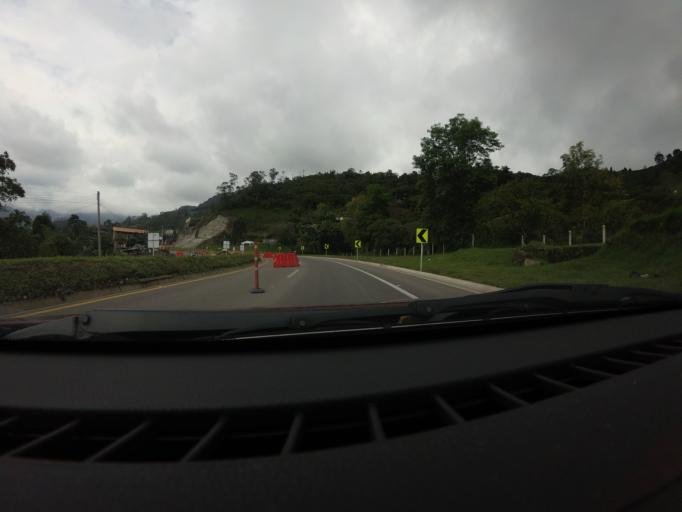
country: CO
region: Cundinamarca
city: San Francisco
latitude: 4.9588
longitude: -74.3031
